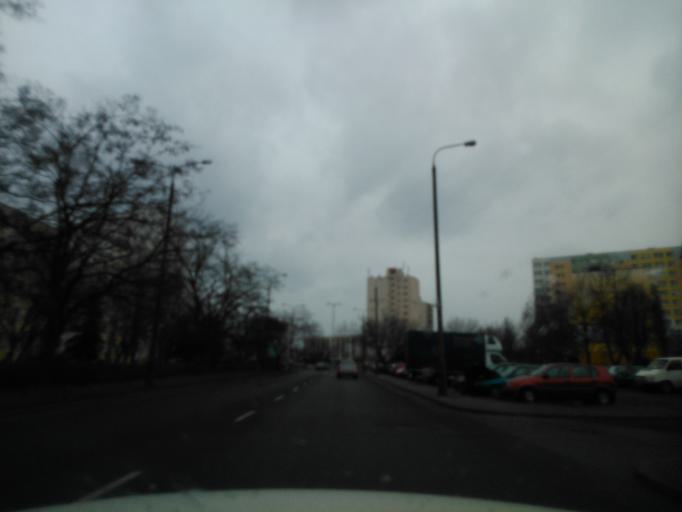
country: PL
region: Kujawsko-Pomorskie
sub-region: Torun
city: Torun
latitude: 53.0285
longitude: 18.6622
